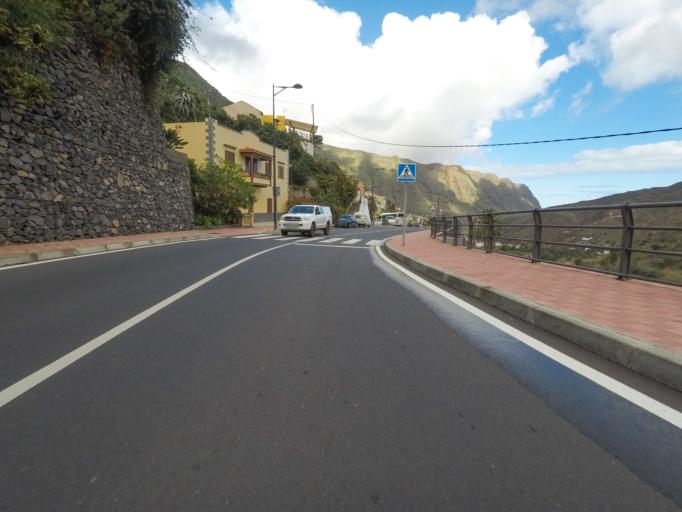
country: ES
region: Canary Islands
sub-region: Provincia de Santa Cruz de Tenerife
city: Hermigua
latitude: 28.1475
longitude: -17.1980
